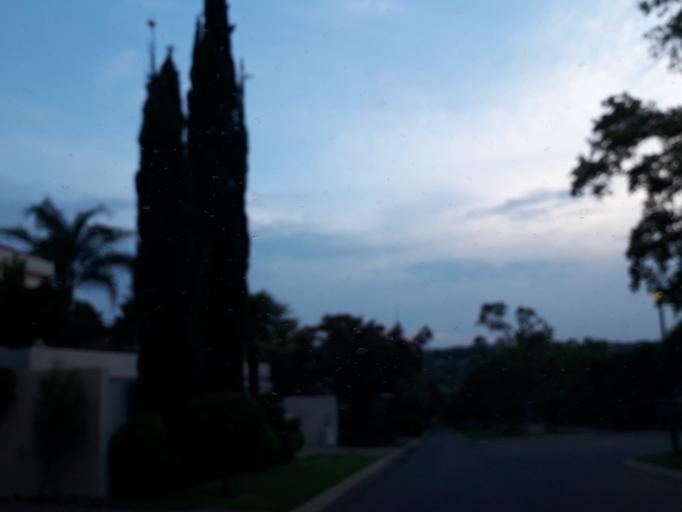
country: ZA
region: Gauteng
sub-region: City of Johannesburg Metropolitan Municipality
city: Diepsloot
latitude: -25.9837
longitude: 28.0001
